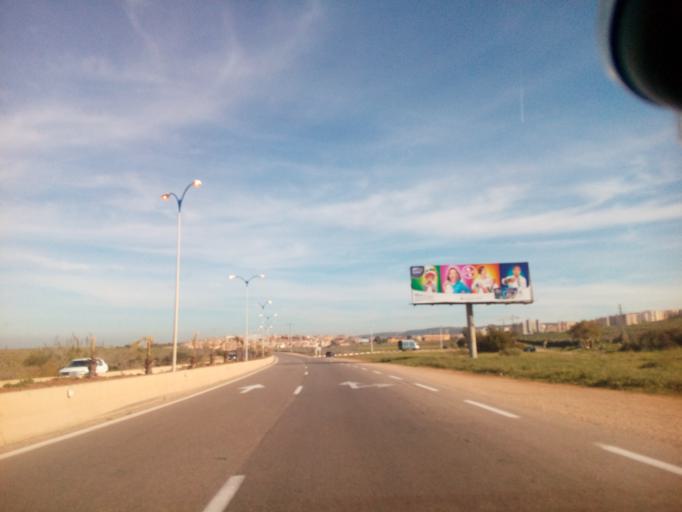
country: DZ
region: Mostaganem
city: Mostaganem
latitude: 35.8231
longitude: -0.0145
